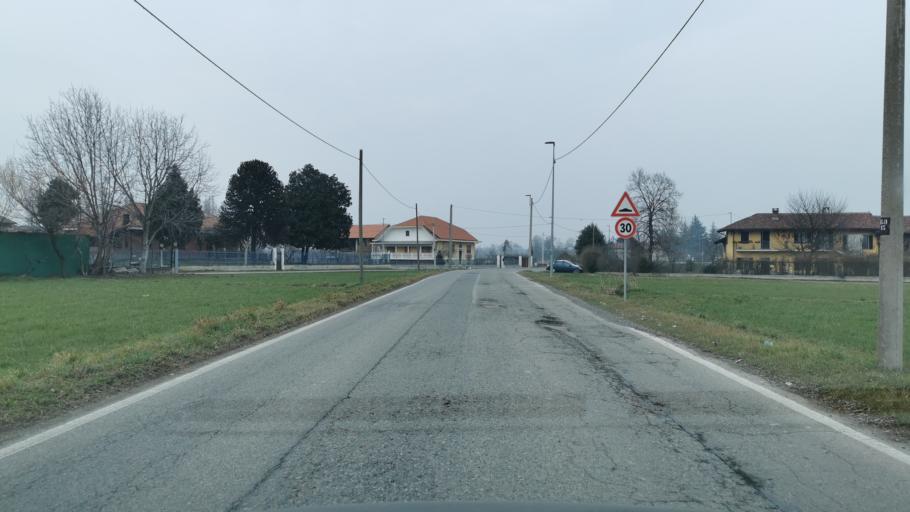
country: IT
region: Piedmont
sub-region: Provincia di Torino
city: Borgaro Torinese
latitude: 45.1230
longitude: 7.6919
